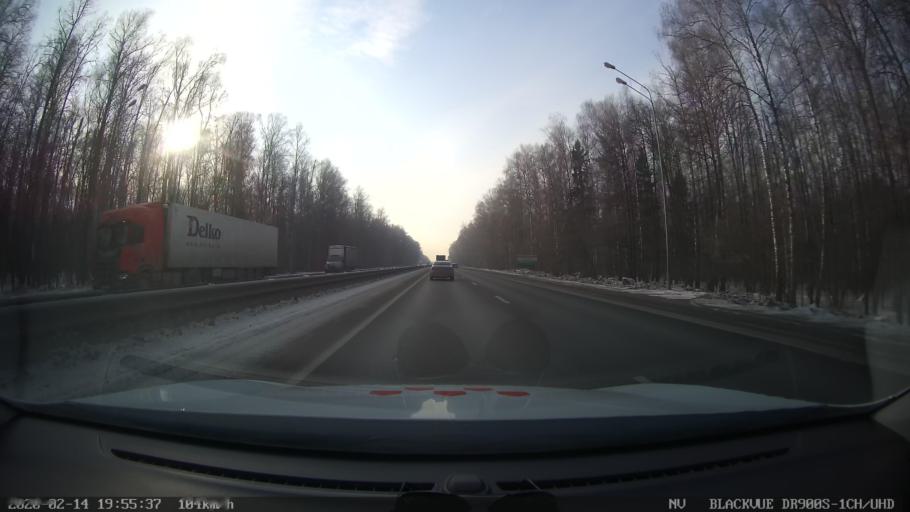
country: RU
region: Tatarstan
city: Osinovo
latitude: 55.8441
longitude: 48.8520
